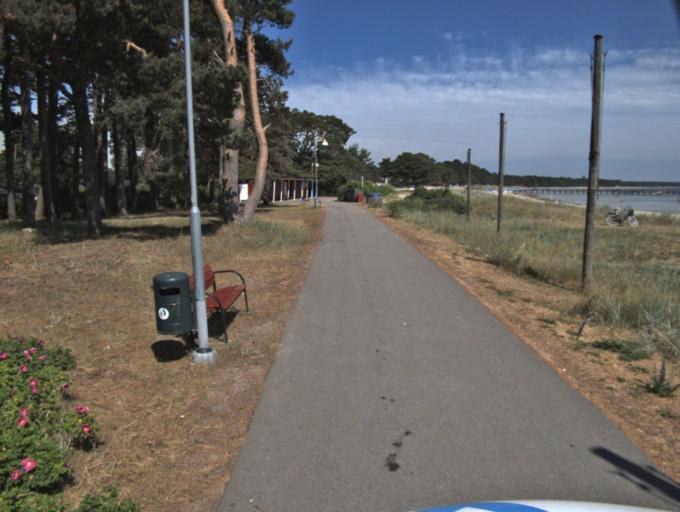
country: SE
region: Skane
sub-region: Kristianstads Kommun
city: Ahus
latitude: 55.9344
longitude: 14.3199
